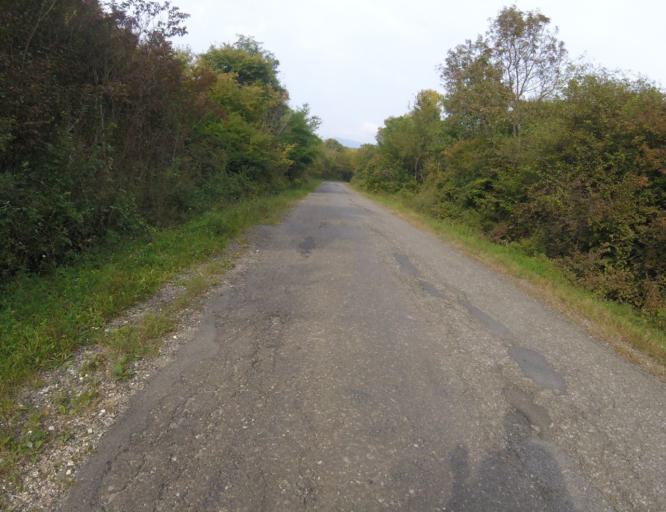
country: HU
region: Pest
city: Veroce
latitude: 47.8432
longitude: 19.0502
